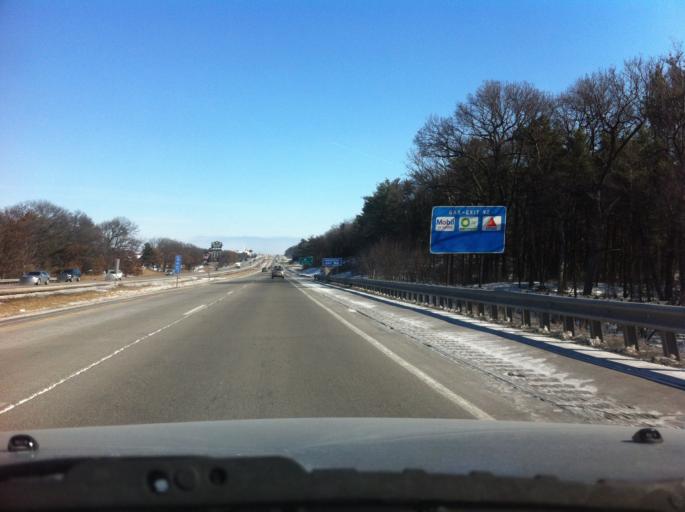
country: US
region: Wisconsin
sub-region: Sauk County
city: Lake Delton
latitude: 43.5886
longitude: -89.8091
